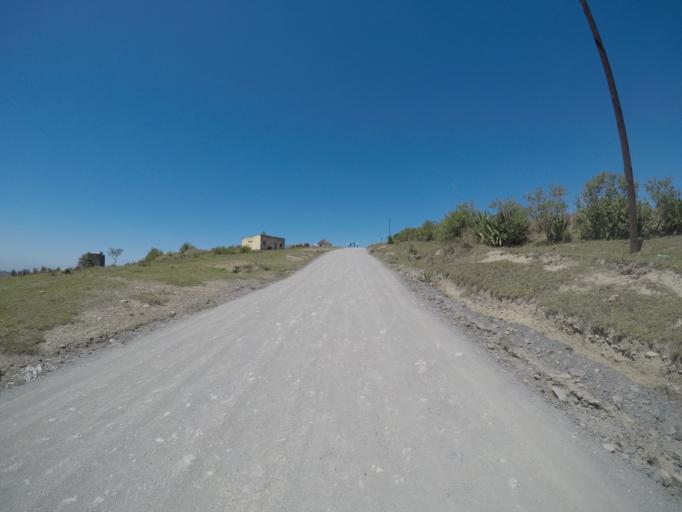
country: ZA
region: Eastern Cape
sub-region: OR Tambo District Municipality
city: Libode
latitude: -31.9815
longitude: 29.0351
